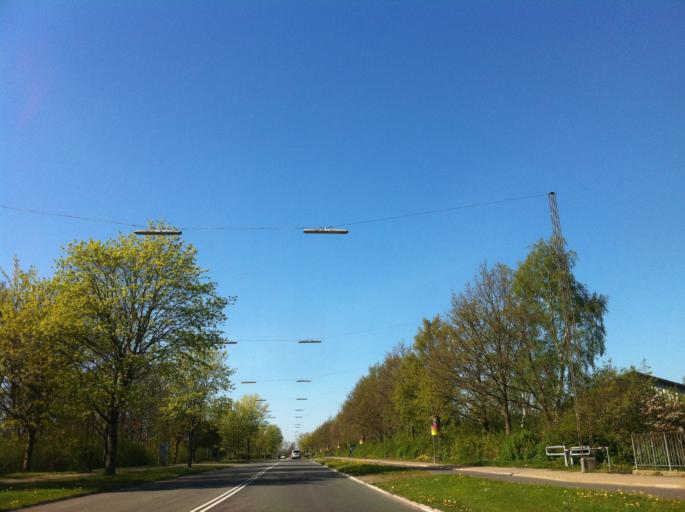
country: DK
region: Zealand
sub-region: Naestved Kommune
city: Naestved
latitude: 55.2047
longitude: 11.7707
